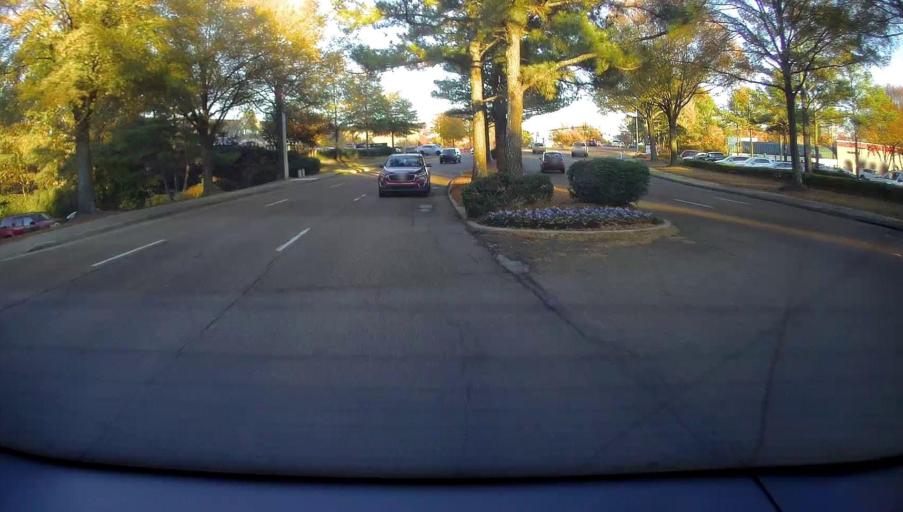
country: US
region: Tennessee
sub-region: Shelby County
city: Germantown
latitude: 35.0957
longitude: -89.8097
